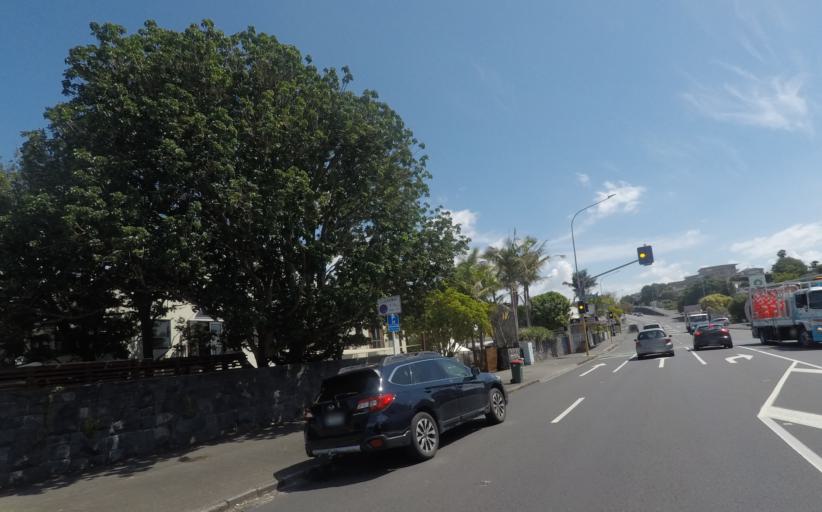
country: NZ
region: Auckland
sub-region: Auckland
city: Tamaki
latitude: -36.8764
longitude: 174.8263
